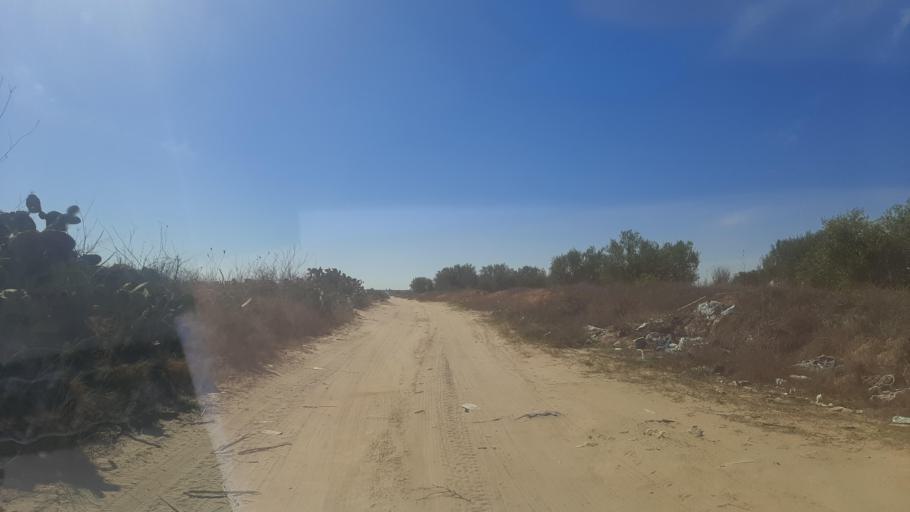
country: TN
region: Safaqis
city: Sfax
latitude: 34.8447
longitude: 10.5608
